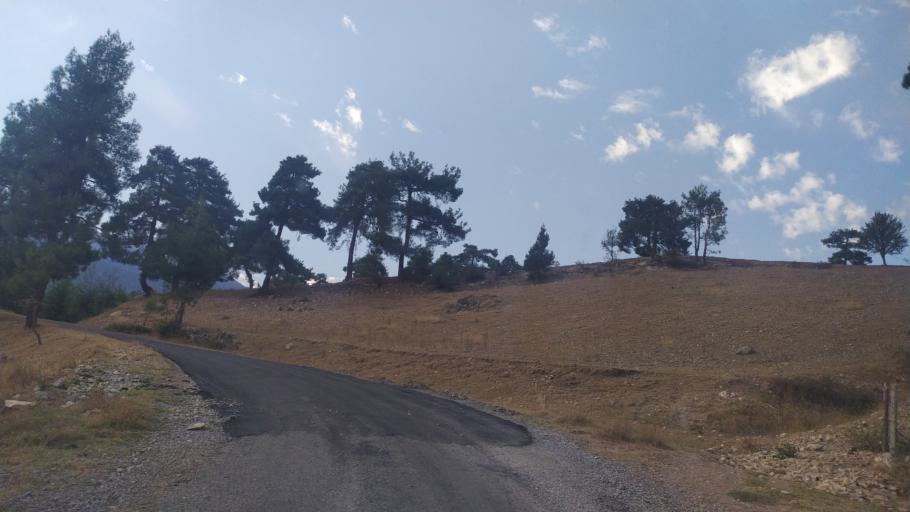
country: TR
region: Mersin
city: Camliyayla
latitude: 37.2216
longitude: 34.7111
